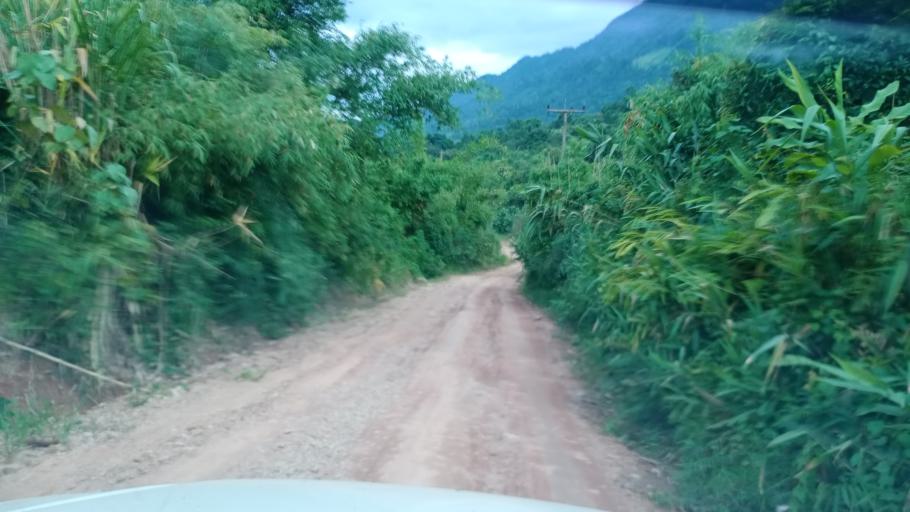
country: TH
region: Changwat Bueng Kan
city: Pak Khat
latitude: 18.7234
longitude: 103.2792
